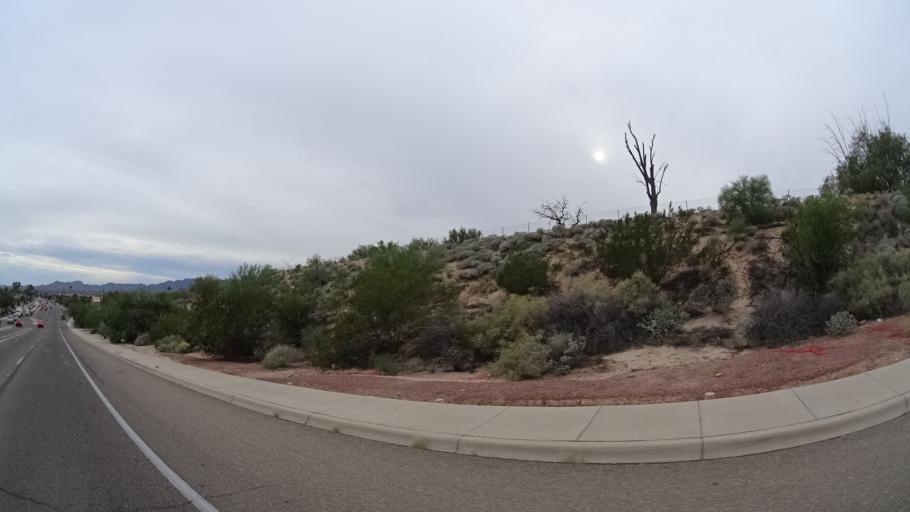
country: US
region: Arizona
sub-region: Pima County
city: Casas Adobes
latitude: 32.3409
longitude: -111.0470
